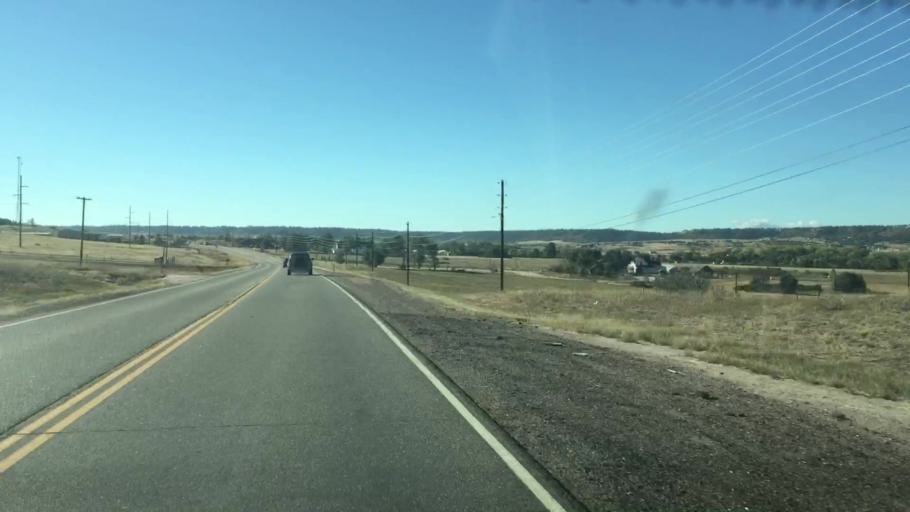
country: US
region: Colorado
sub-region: Douglas County
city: The Pinery
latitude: 39.4128
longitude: -104.7610
